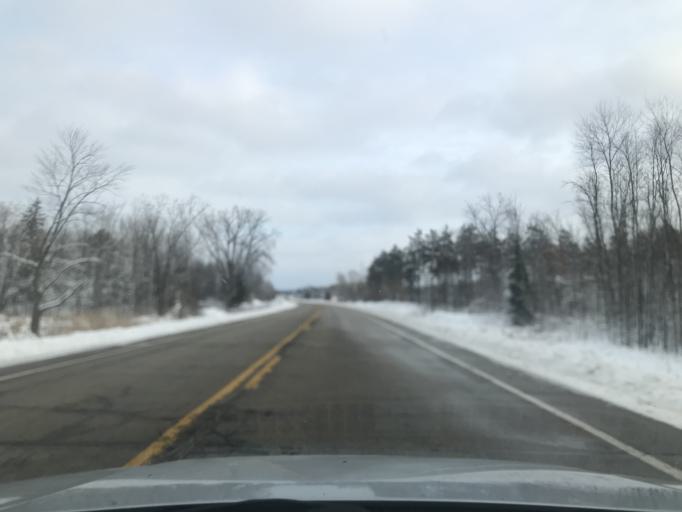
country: US
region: Wisconsin
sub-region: Oconto County
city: Oconto Falls
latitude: 44.8867
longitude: -88.0362
